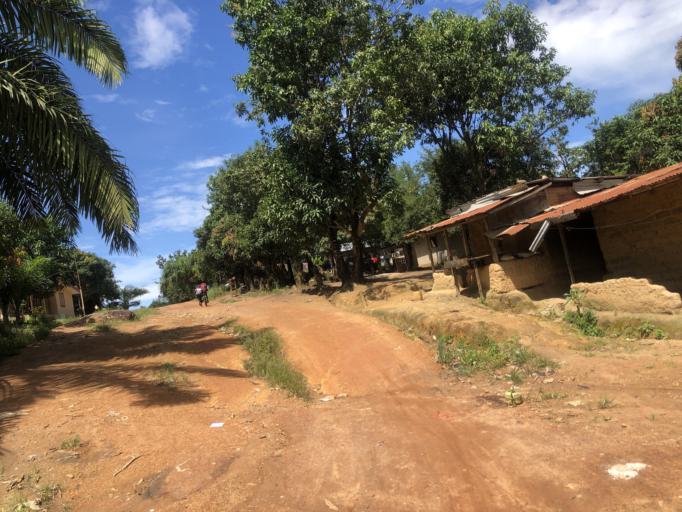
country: SL
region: Eastern Province
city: Koidu
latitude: 8.6407
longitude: -10.9498
